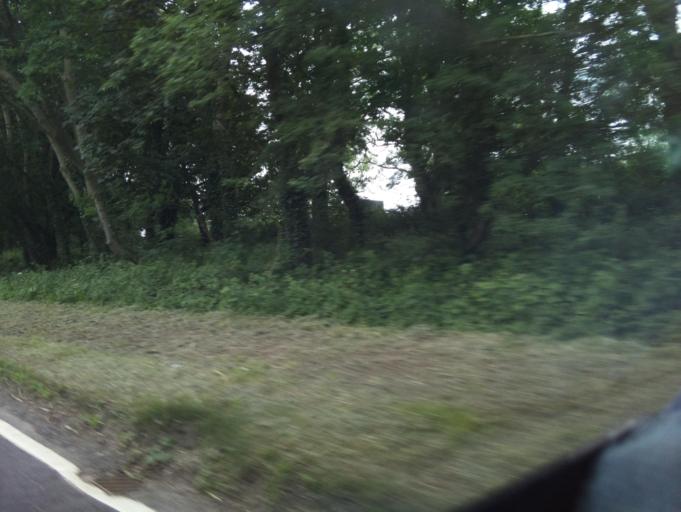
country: GB
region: England
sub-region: Leicestershire
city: Grimston
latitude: 52.7913
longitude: -1.0260
